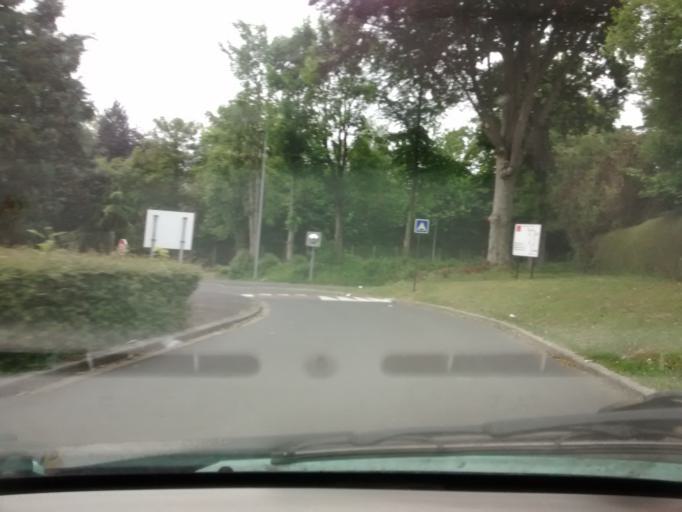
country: FR
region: Lower Normandy
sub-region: Departement de la Manche
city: Saint-Lo
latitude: 49.1088
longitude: -1.0701
